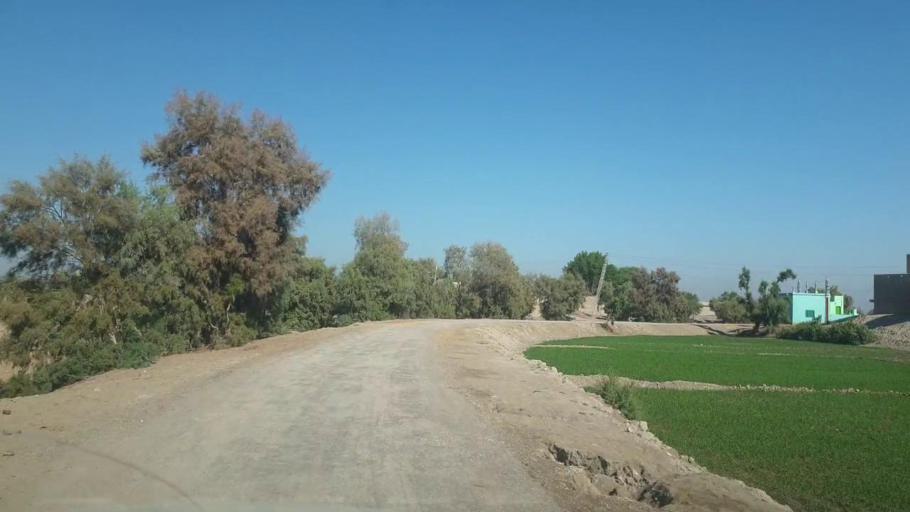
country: PK
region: Sindh
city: Bhan
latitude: 26.5246
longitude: 67.6423
